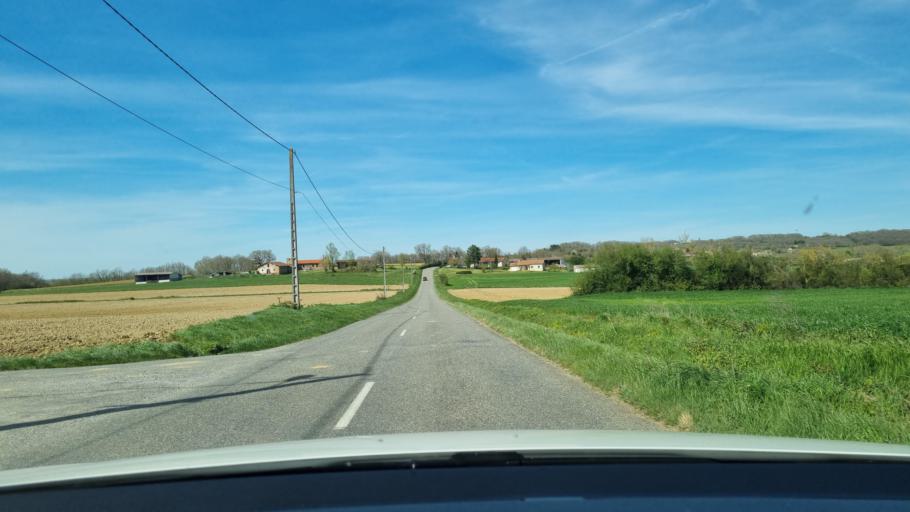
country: FR
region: Midi-Pyrenees
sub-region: Departement de la Haute-Garonne
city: Rieumes
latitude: 43.4733
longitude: 1.0632
